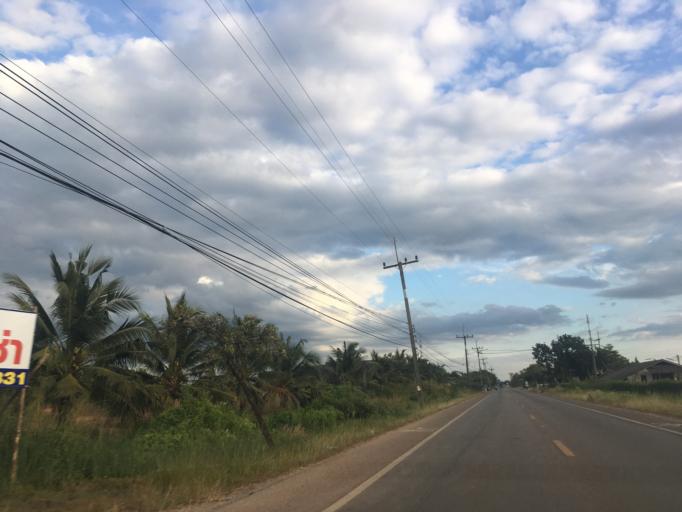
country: TH
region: Chanthaburi
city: Na Yai Am
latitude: 12.7130
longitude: 101.7717
